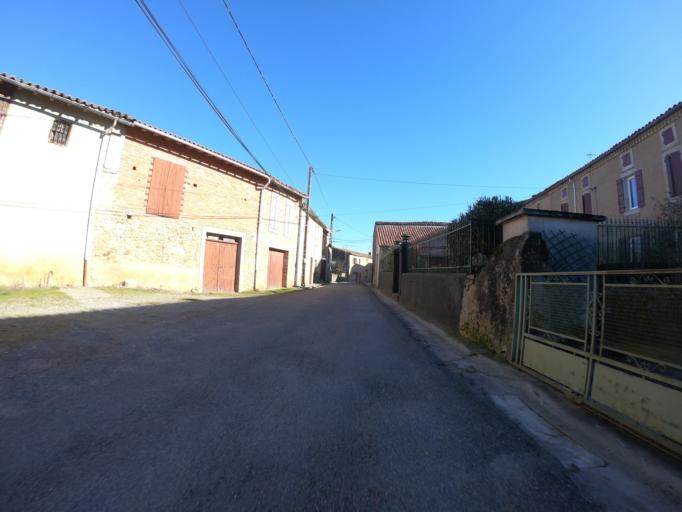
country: FR
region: Midi-Pyrenees
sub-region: Departement de l'Ariege
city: La Tour-du-Crieu
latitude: 43.0972
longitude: 1.7371
